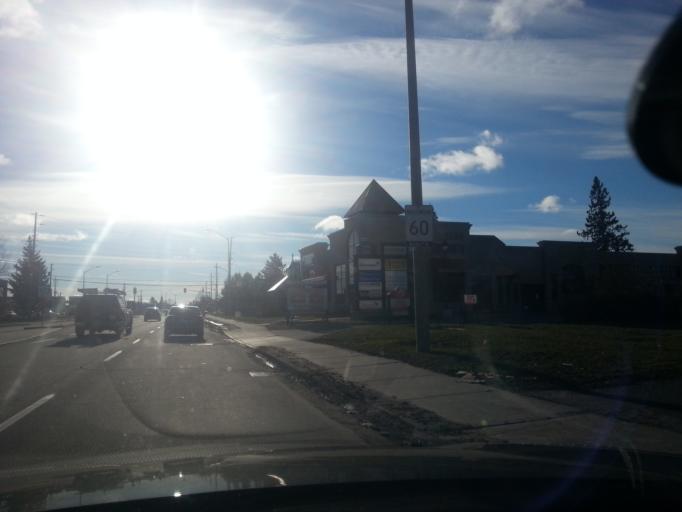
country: CA
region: Ontario
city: Ottawa
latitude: 45.3325
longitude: -75.7229
